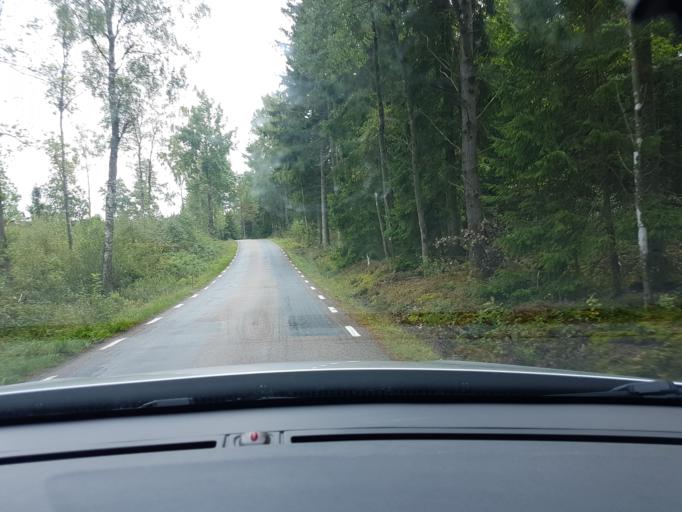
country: SE
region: Vaestra Goetaland
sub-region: Ale Kommun
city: Alvangen
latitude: 57.9017
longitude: 12.1825
